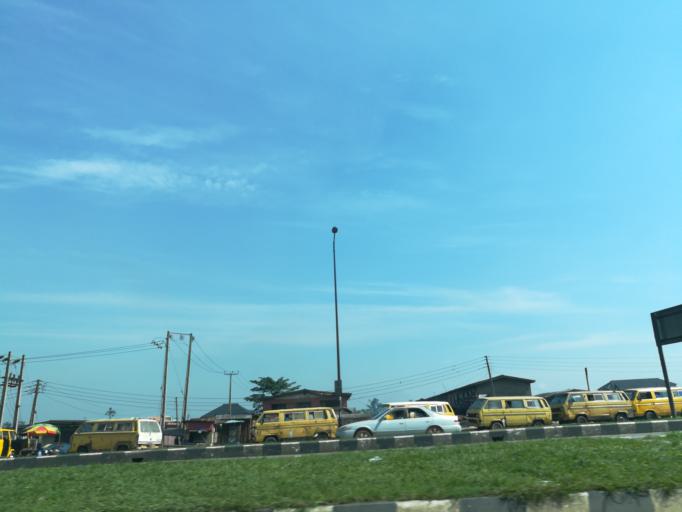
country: NG
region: Lagos
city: Ojota
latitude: 6.6094
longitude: 3.4298
